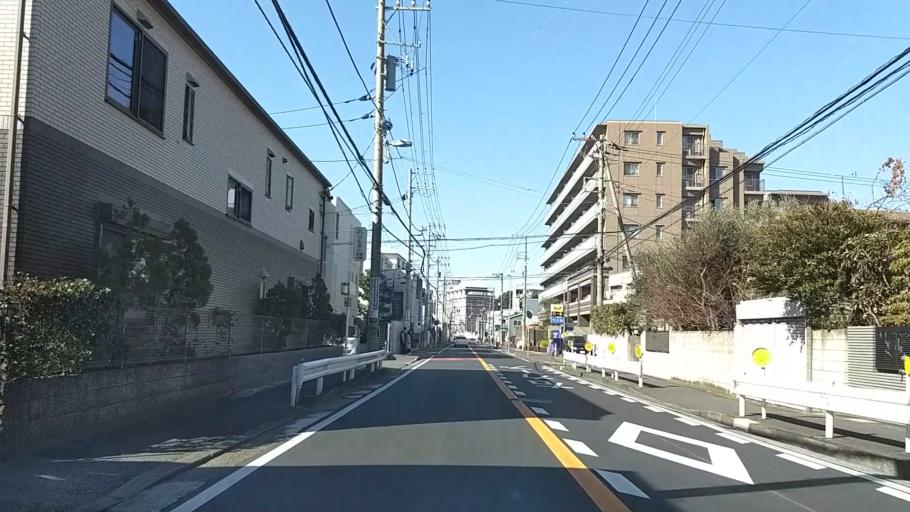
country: JP
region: Kanagawa
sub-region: Kawasaki-shi
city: Kawasaki
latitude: 35.5145
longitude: 139.6563
